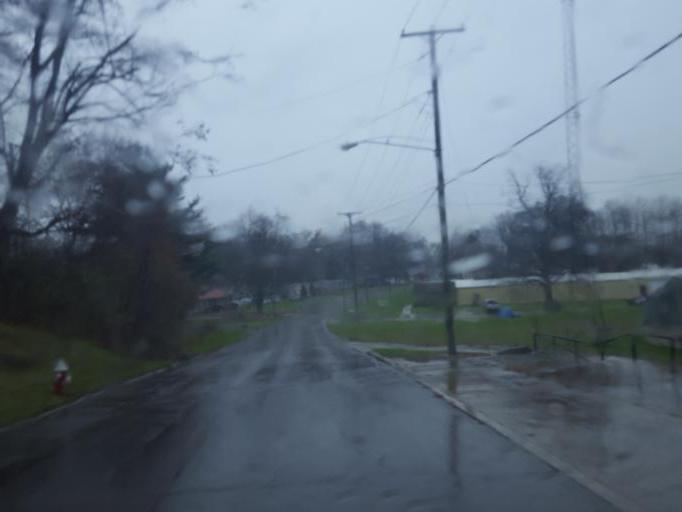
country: US
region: Ohio
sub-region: Richland County
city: Lexington
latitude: 40.6747
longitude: -82.5800
